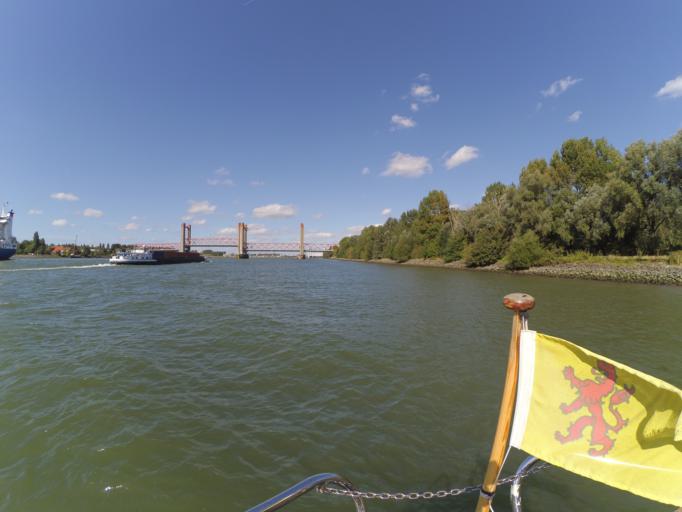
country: NL
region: South Holland
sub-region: Gemeente Spijkenisse
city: Spijkenisse
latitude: 51.8564
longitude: 4.3456
